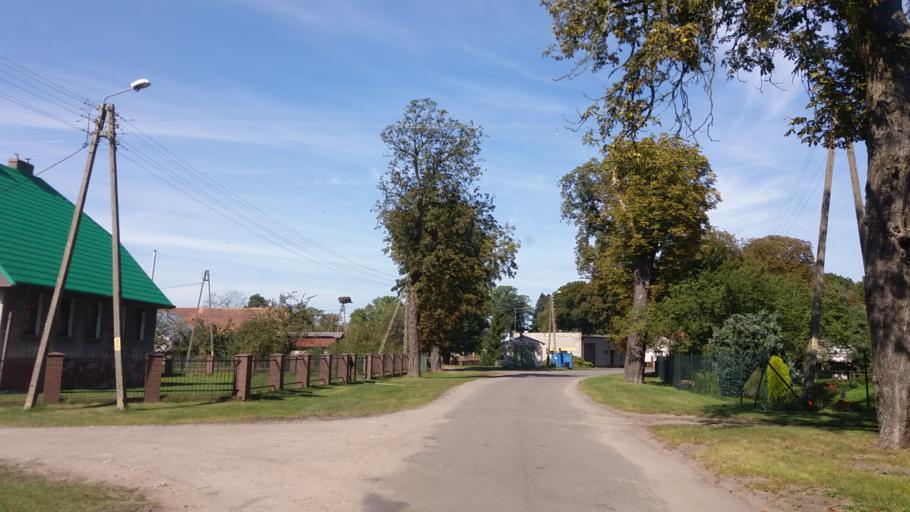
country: PL
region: West Pomeranian Voivodeship
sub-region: Powiat choszczenski
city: Choszczno
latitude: 53.1043
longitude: 15.4074
